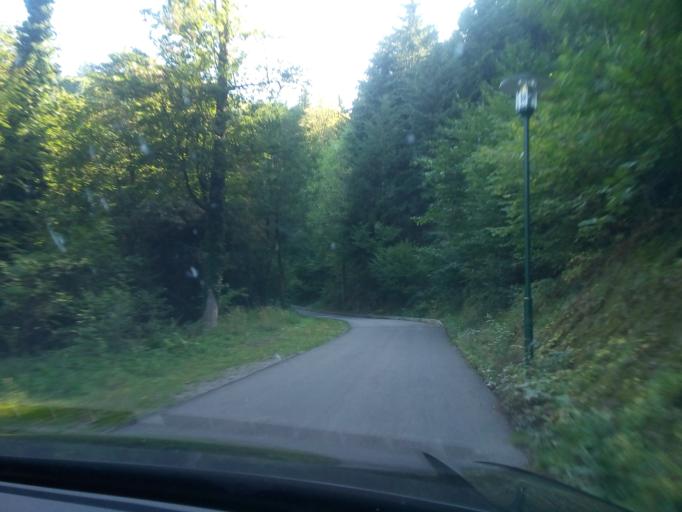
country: DE
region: Baden-Wuerttemberg
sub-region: Freiburg Region
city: Oberkirch
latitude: 48.5377
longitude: 8.0924
